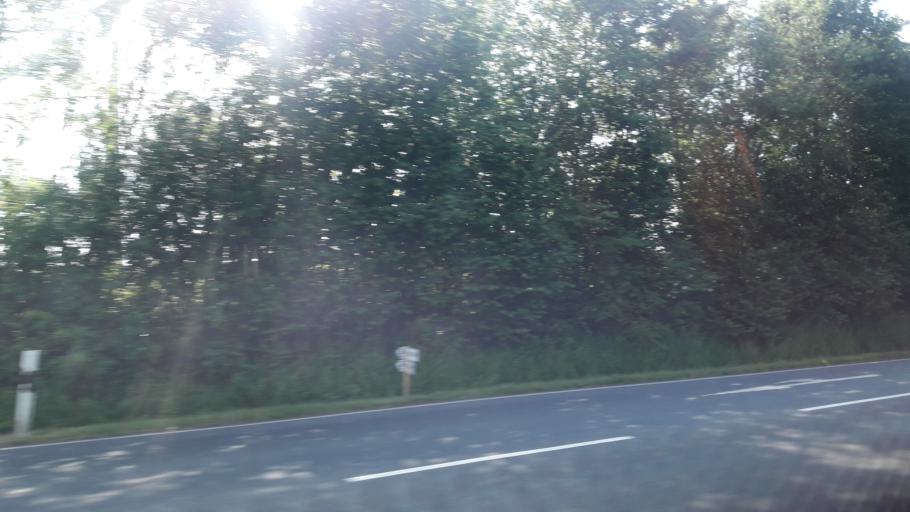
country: DE
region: North Rhine-Westphalia
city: Lichtenau
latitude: 51.6355
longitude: 8.8762
